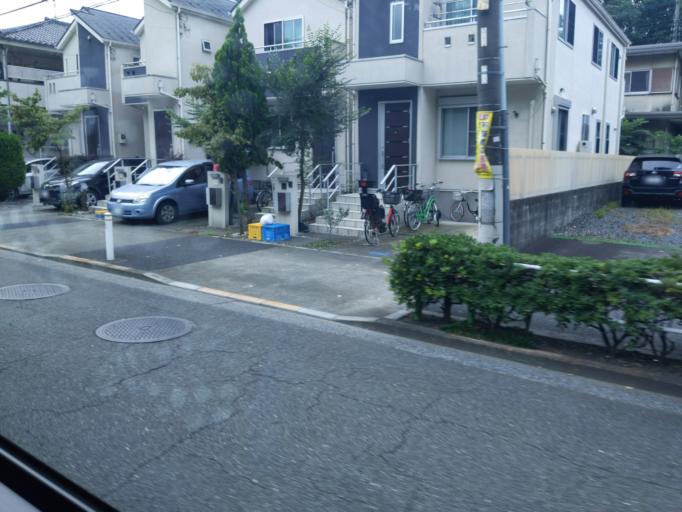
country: JP
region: Saitama
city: Wako
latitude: 35.7875
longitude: 139.6502
